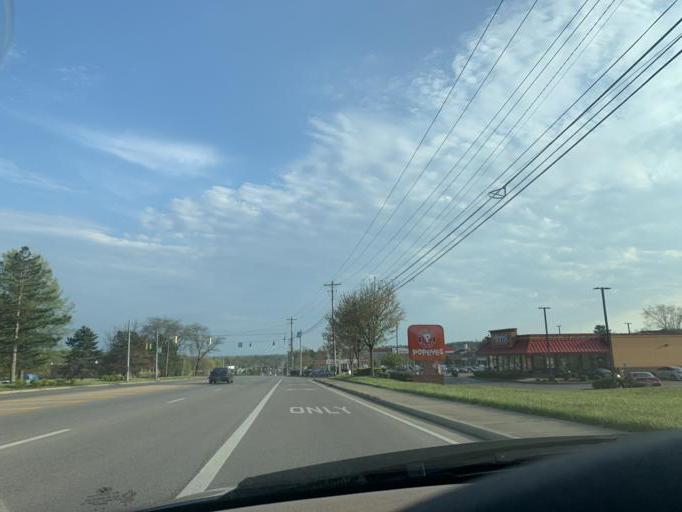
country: US
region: Ohio
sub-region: Hamilton County
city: Woodlawn
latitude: 39.2613
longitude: -84.4696
